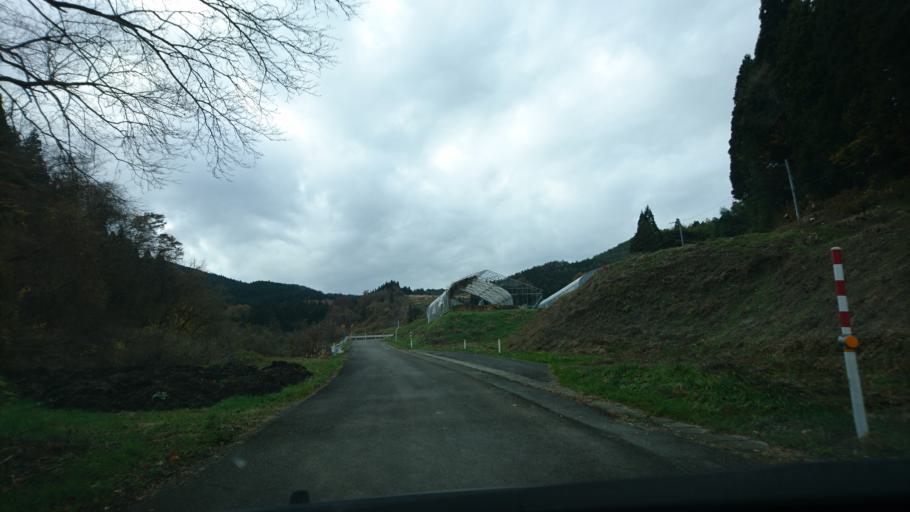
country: JP
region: Iwate
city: Ichinoseki
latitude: 39.0055
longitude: 141.2100
